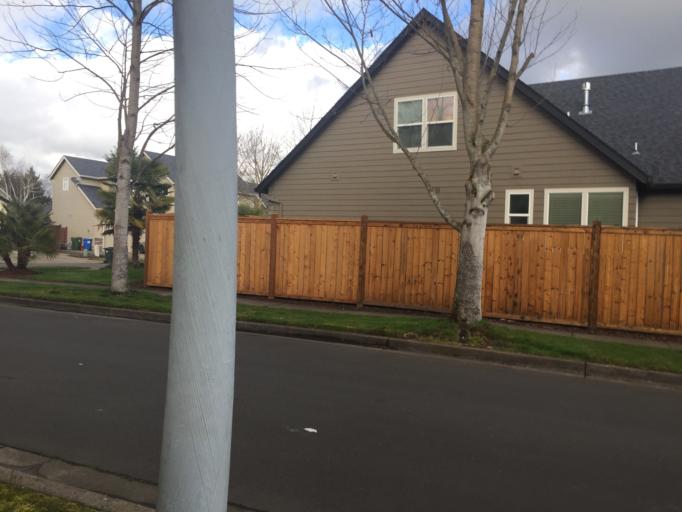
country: US
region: Oregon
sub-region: Lane County
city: Eugene
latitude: 44.1018
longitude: -123.1568
